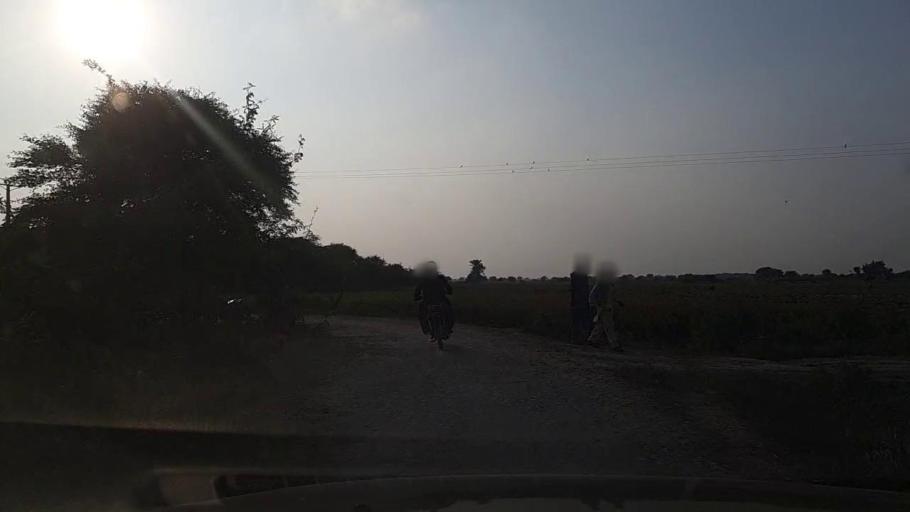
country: PK
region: Sindh
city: Jati
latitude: 24.5385
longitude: 68.3413
